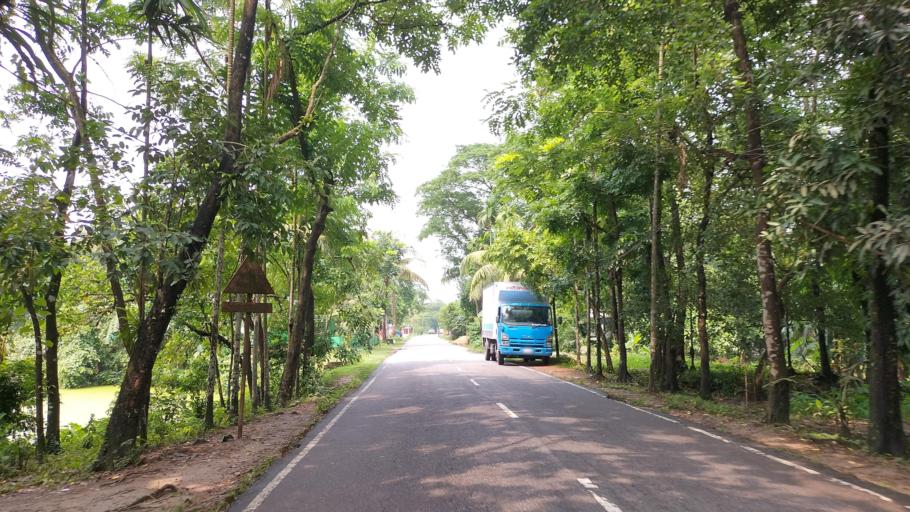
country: BD
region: Dhaka
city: Netrakona
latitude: 24.9032
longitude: 90.7631
